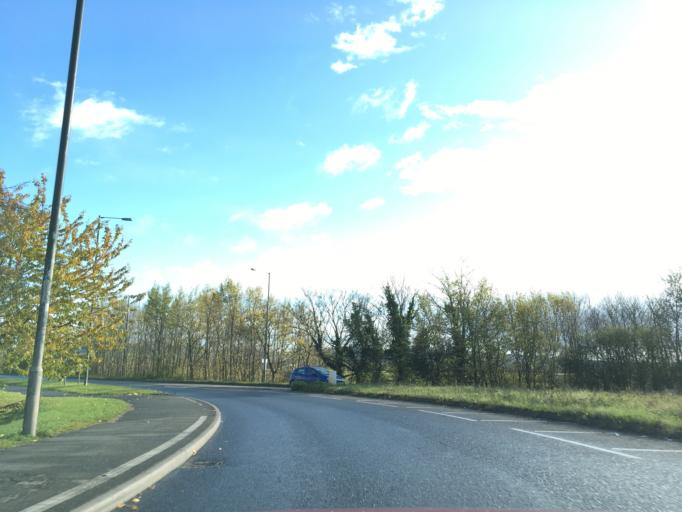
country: GB
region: England
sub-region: Worcestershire
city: Bredon
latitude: 51.9967
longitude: -2.1221
